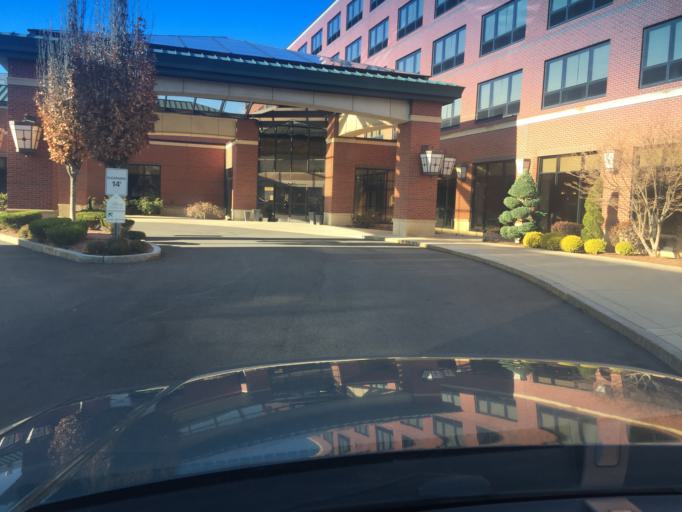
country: US
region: Massachusetts
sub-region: Norfolk County
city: Norwood
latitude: 42.1753
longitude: -71.1950
